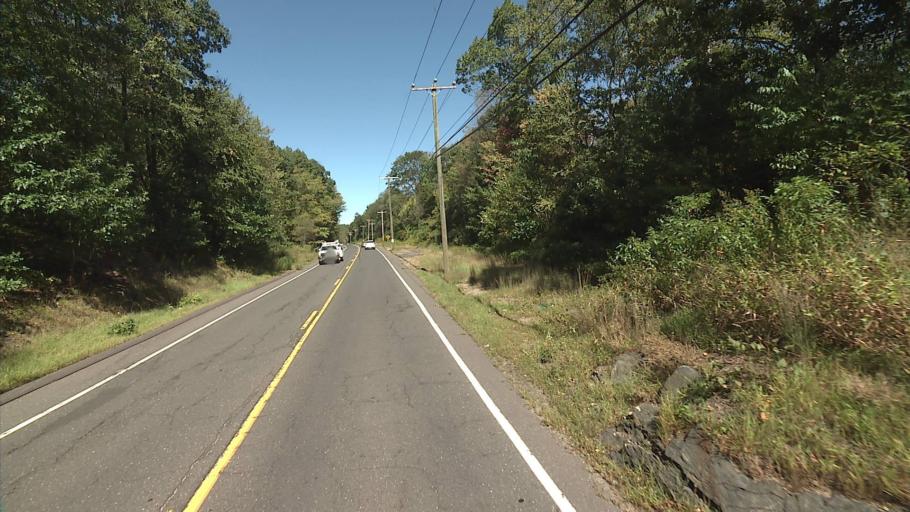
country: US
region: Connecticut
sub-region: New Haven County
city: Prospect
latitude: 41.4818
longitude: -72.9707
